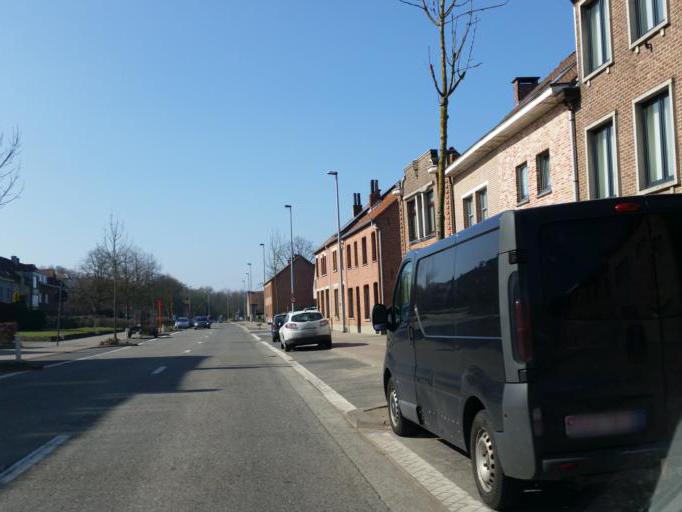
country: BE
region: Flanders
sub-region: Provincie Antwerpen
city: Bornem
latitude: 51.1297
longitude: 4.2630
